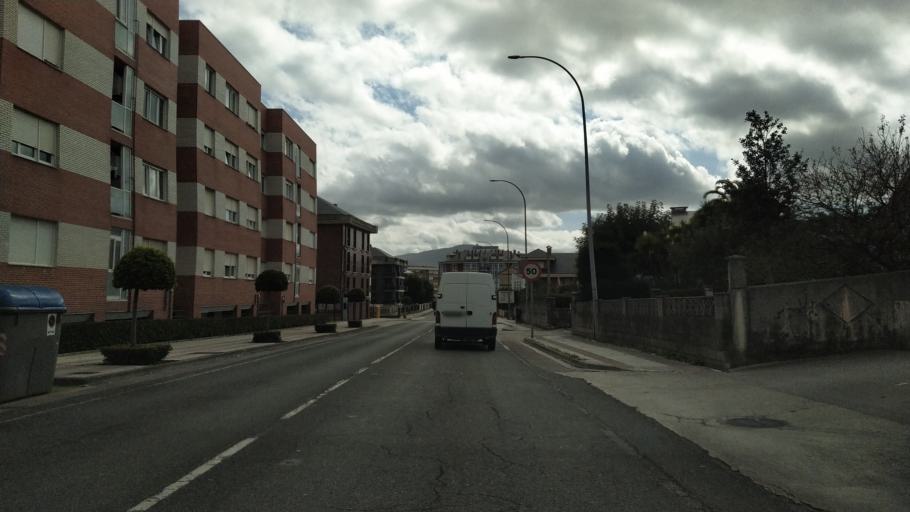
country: ES
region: Cantabria
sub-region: Provincia de Cantabria
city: El Astillero
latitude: 43.4213
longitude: -3.8483
